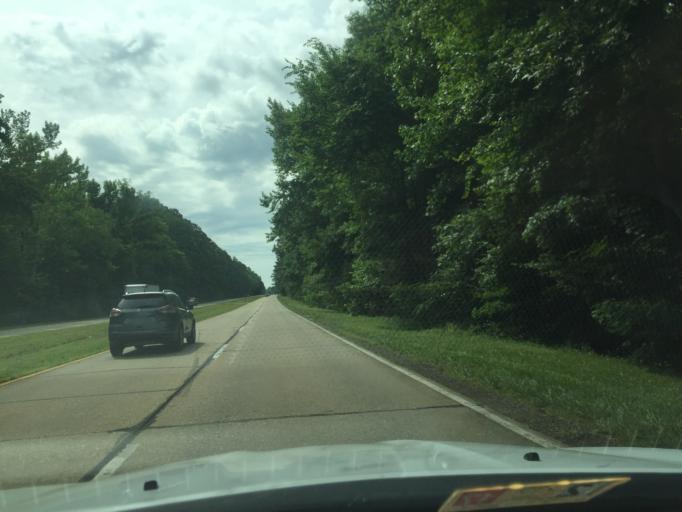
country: US
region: Virginia
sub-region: Charles City County
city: Charles City
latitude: 37.4673
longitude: -77.1098
